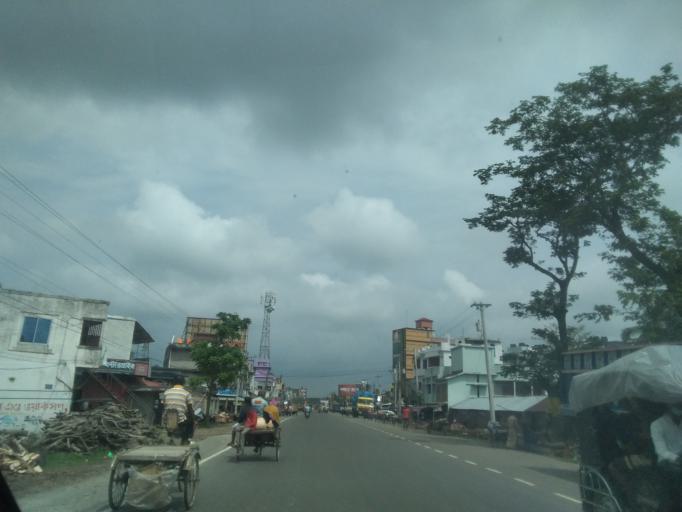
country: BD
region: Khulna
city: Kesabpur
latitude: 22.8394
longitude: 89.2981
